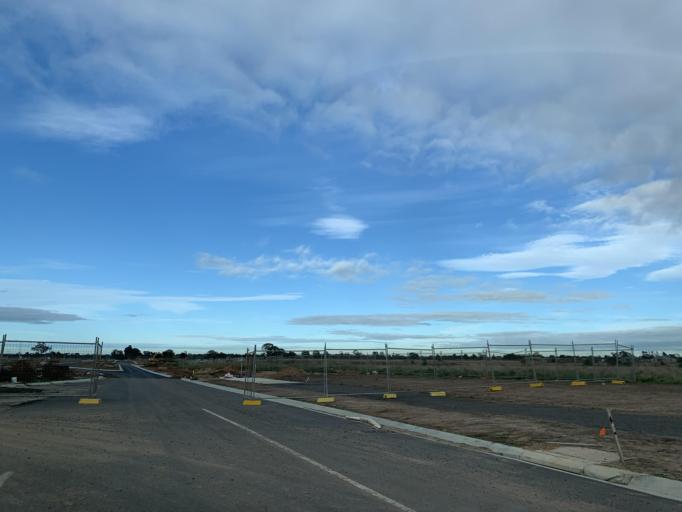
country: AU
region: Victoria
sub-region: Cardinia
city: Officer South
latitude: -38.1273
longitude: 145.3640
